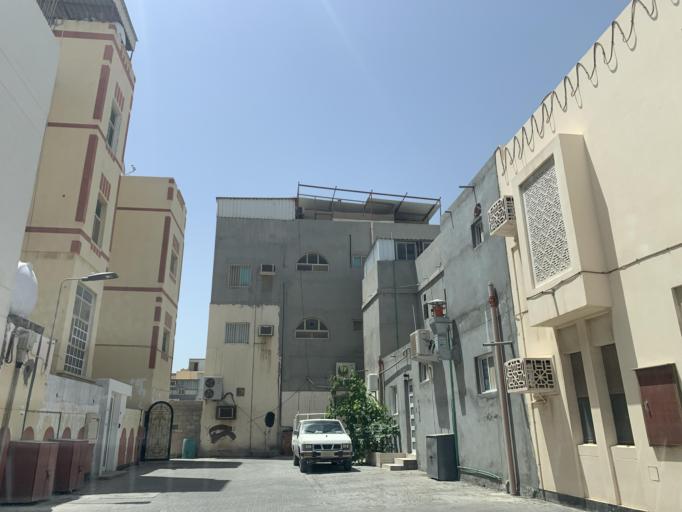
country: BH
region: Northern
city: Sitrah
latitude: 26.1581
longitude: 50.6209
